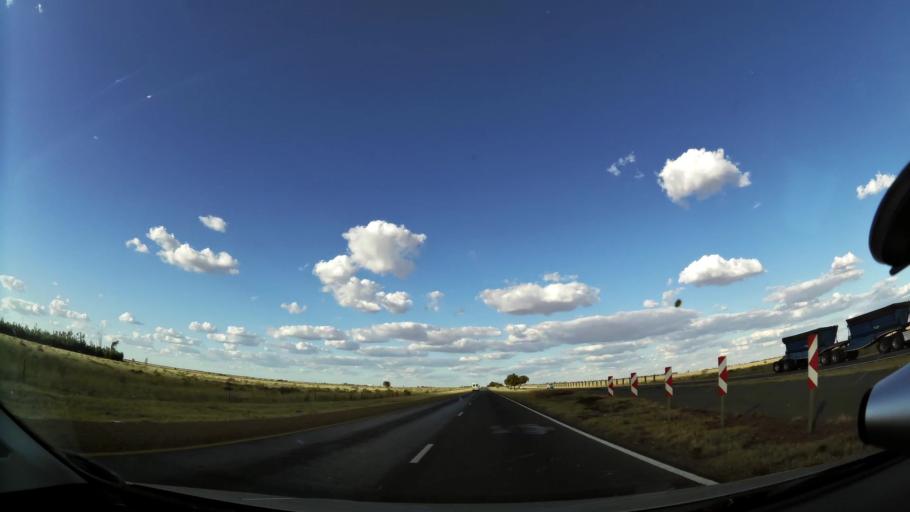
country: ZA
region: North-West
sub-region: Dr Kenneth Kaunda District Municipality
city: Klerksdorp
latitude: -26.8468
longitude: 26.7133
